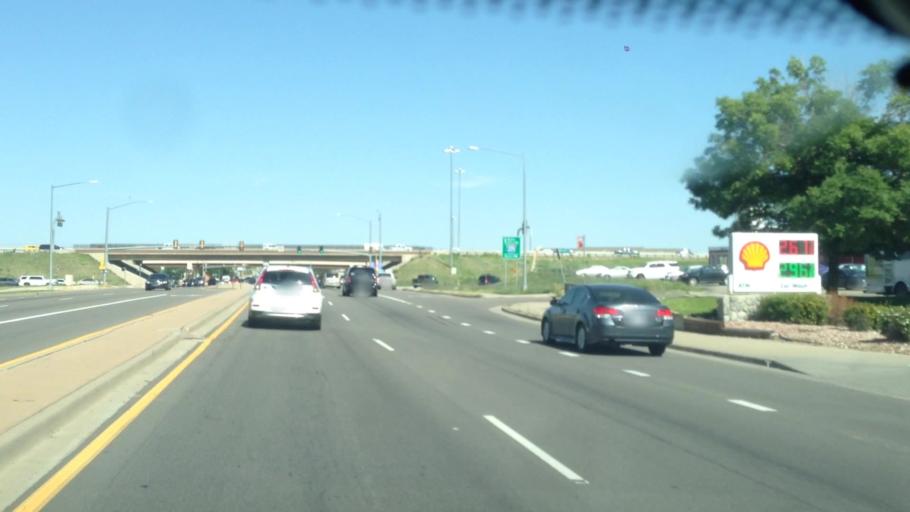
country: US
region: Colorado
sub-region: Adams County
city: Aurora
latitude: 39.7256
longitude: -104.8276
